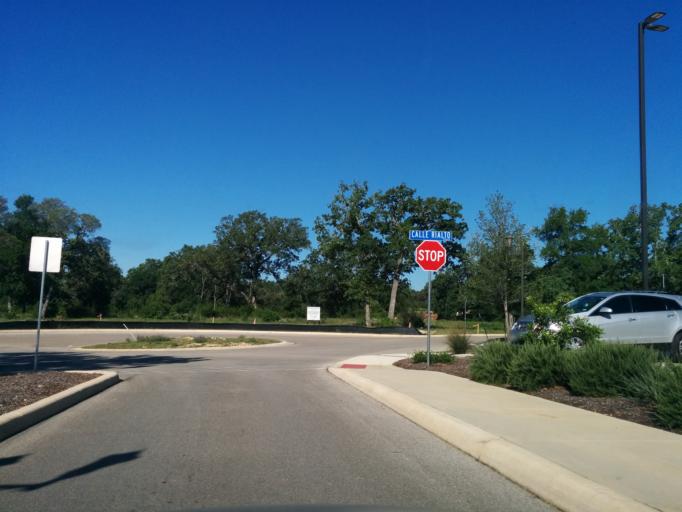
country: US
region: Texas
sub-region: Bexar County
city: Cross Mountain
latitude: 29.6755
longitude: -98.6374
